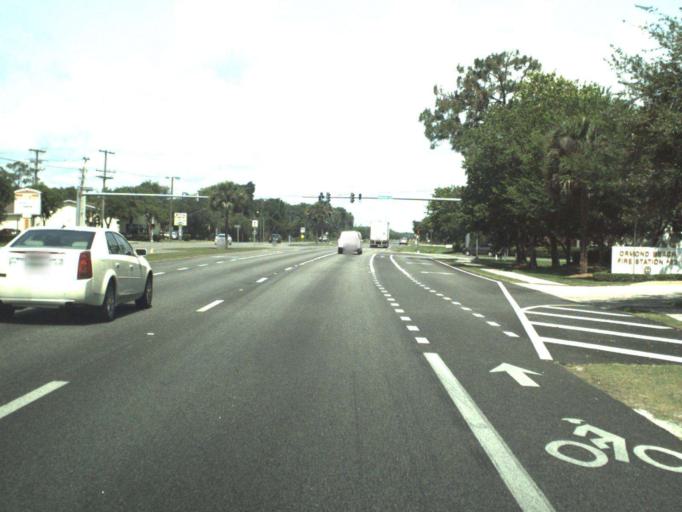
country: US
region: Florida
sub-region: Volusia County
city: Ormond Beach
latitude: 29.2902
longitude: -81.0684
